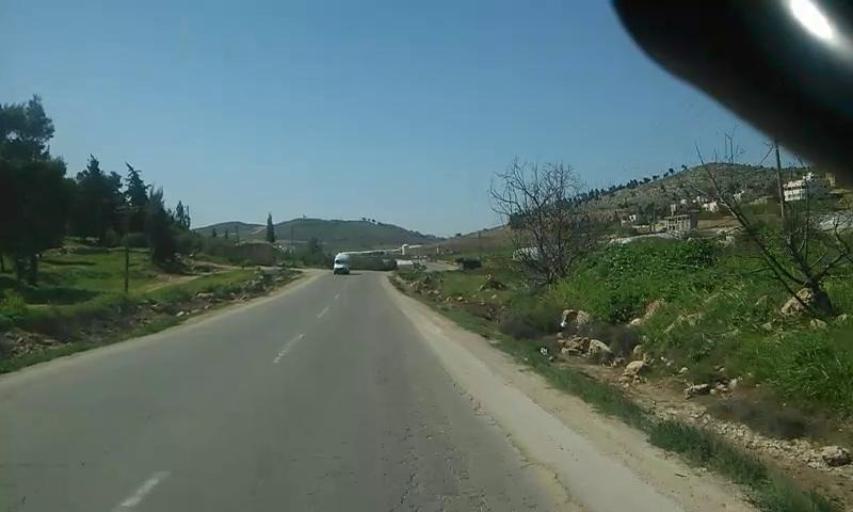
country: PS
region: West Bank
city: Ar Rihiyah
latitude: 31.4867
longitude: 35.0588
